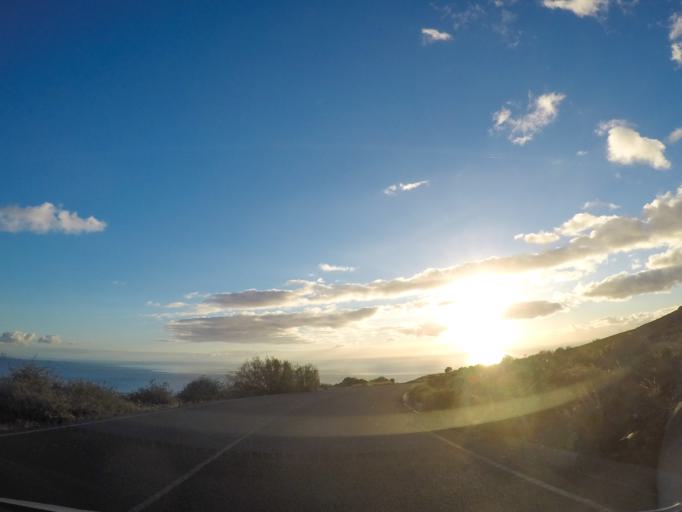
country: ES
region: Canary Islands
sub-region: Provincia de Santa Cruz de Tenerife
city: Alajero
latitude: 28.0351
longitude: -17.2207
